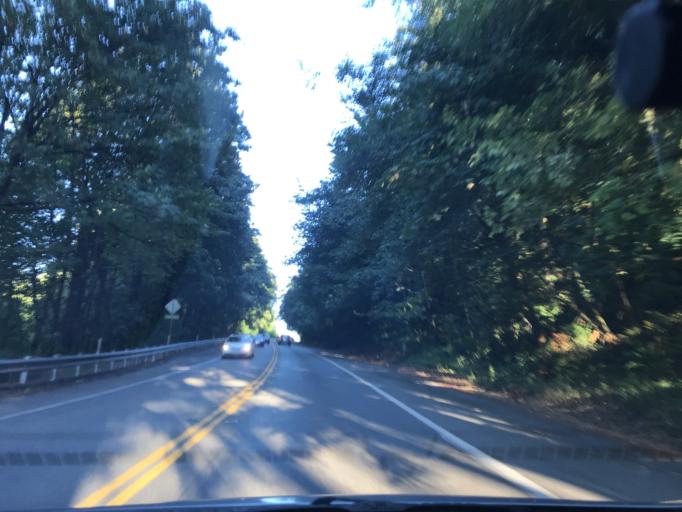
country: US
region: Washington
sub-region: King County
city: Pacific
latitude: 47.2605
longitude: -122.1914
